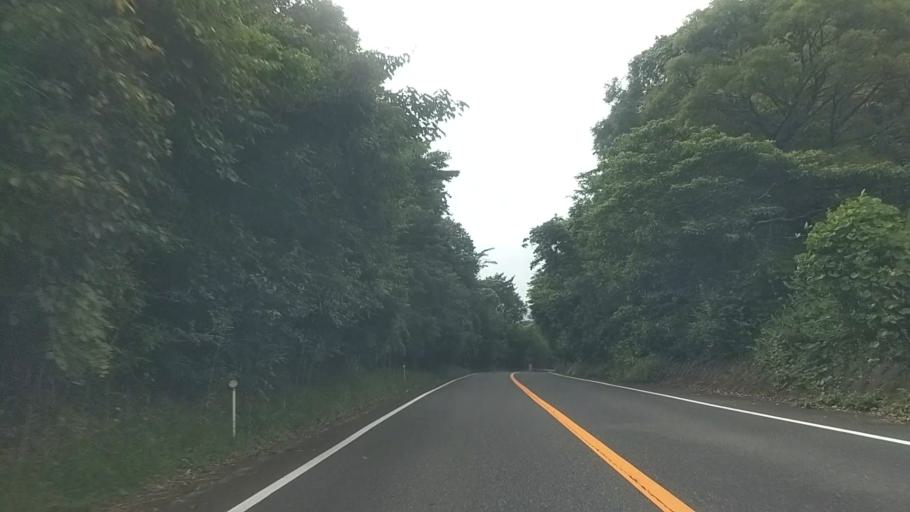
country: JP
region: Chiba
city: Kimitsu
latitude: 35.2345
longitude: 140.0098
